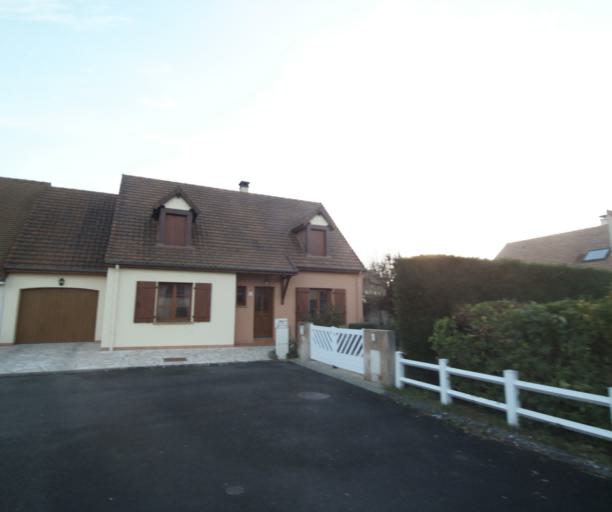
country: FR
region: Pays de la Loire
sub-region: Departement de la Sarthe
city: Le Mans
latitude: 47.9671
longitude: 0.2170
